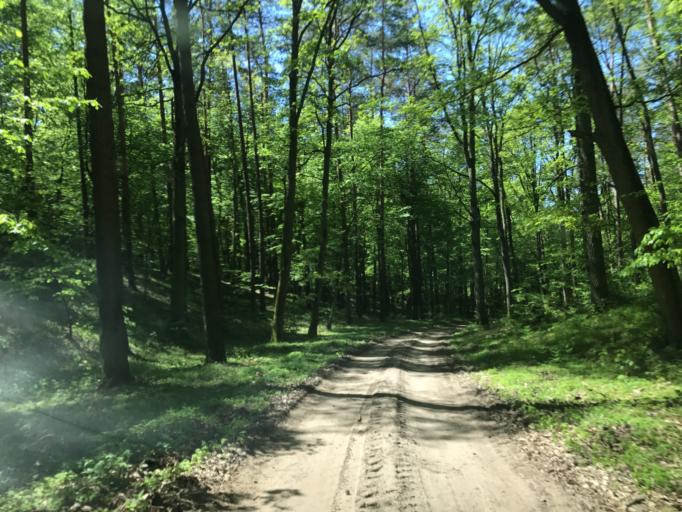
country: PL
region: Kujawsko-Pomorskie
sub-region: Powiat brodnicki
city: Gorzno
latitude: 53.2151
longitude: 19.6744
